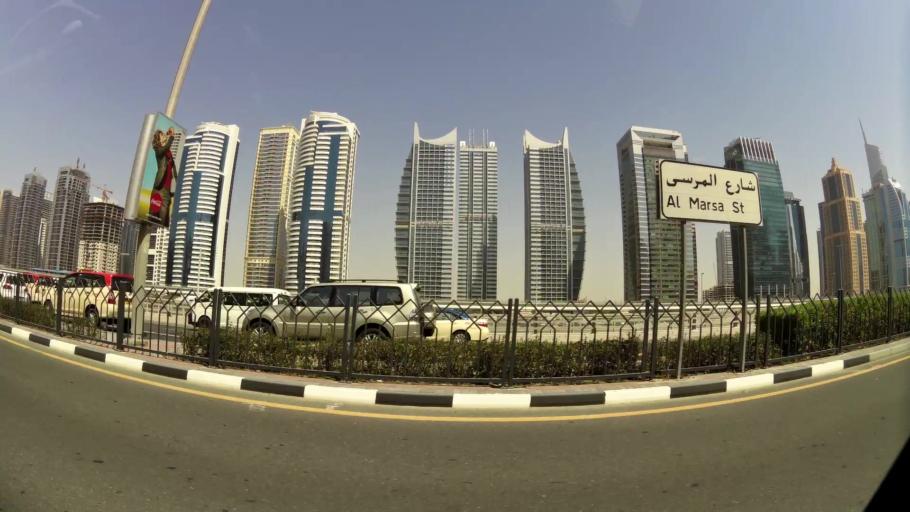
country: AE
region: Dubai
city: Dubai
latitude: 25.0773
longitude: 55.1425
